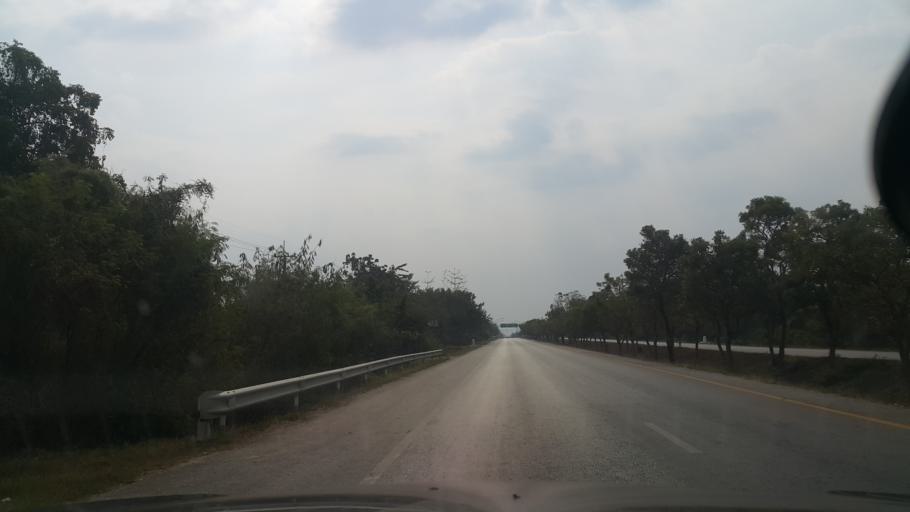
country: TH
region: Sukhothai
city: Sukhothai
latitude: 17.0574
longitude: 99.8991
